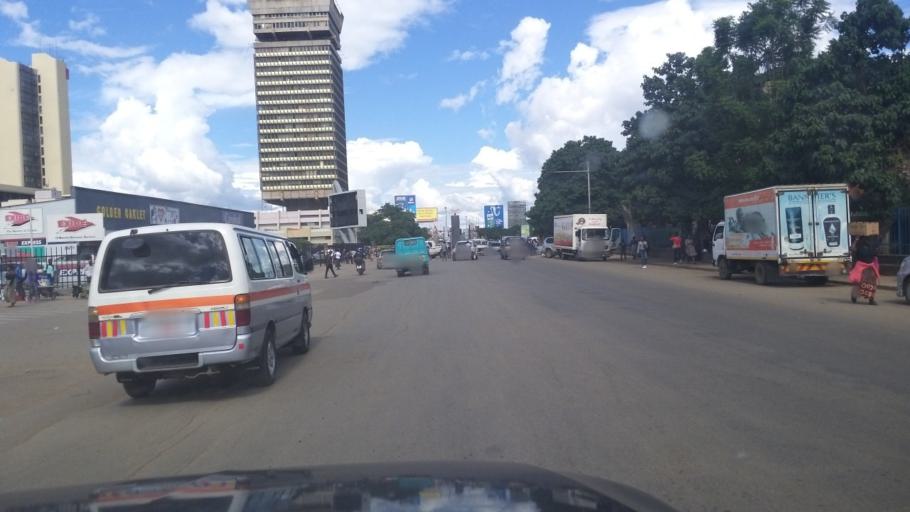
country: ZM
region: Lusaka
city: Lusaka
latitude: -15.4251
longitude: 28.2816
